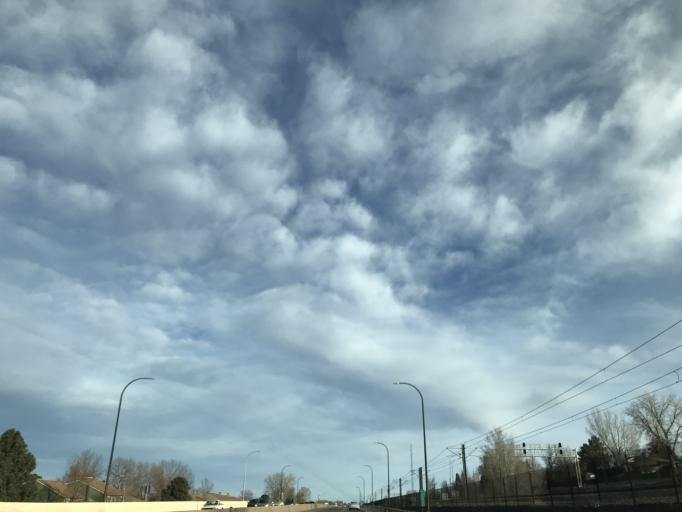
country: US
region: Colorado
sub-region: Arapahoe County
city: Columbine Valley
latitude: 39.5867
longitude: -105.0229
